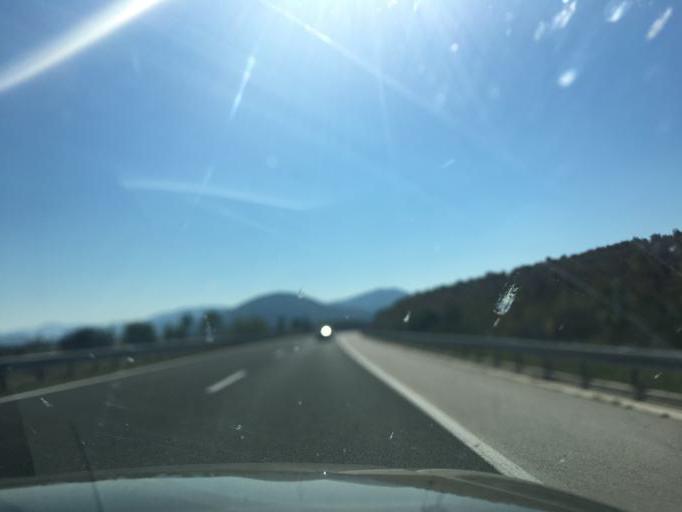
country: HR
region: Splitsko-Dalmatinska
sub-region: Grad Trogir
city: Trogir
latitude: 43.6543
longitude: 16.1961
